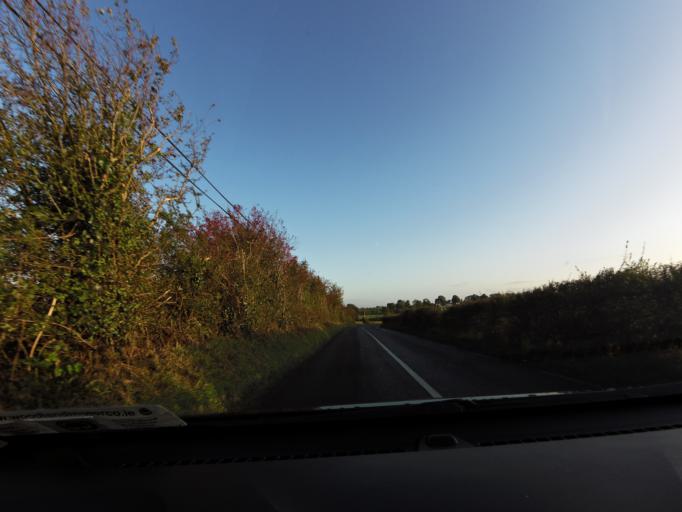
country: IE
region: Connaught
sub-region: Roscommon
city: Castlerea
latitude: 53.6884
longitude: -8.5663
